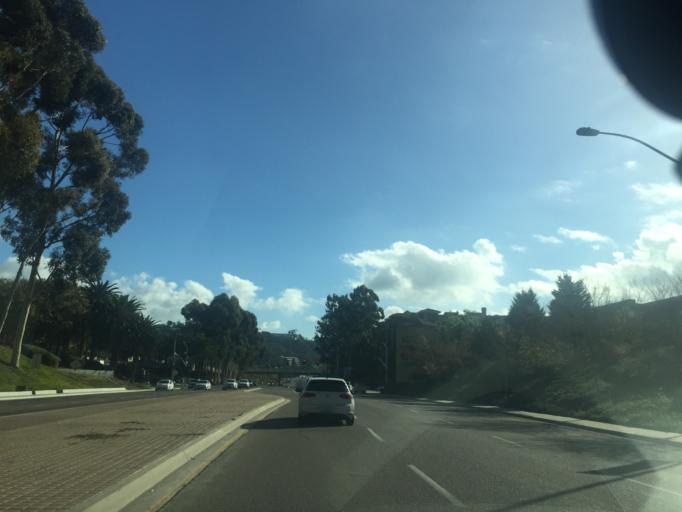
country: US
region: California
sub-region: San Diego County
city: San Diego
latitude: 32.7769
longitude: -117.1416
